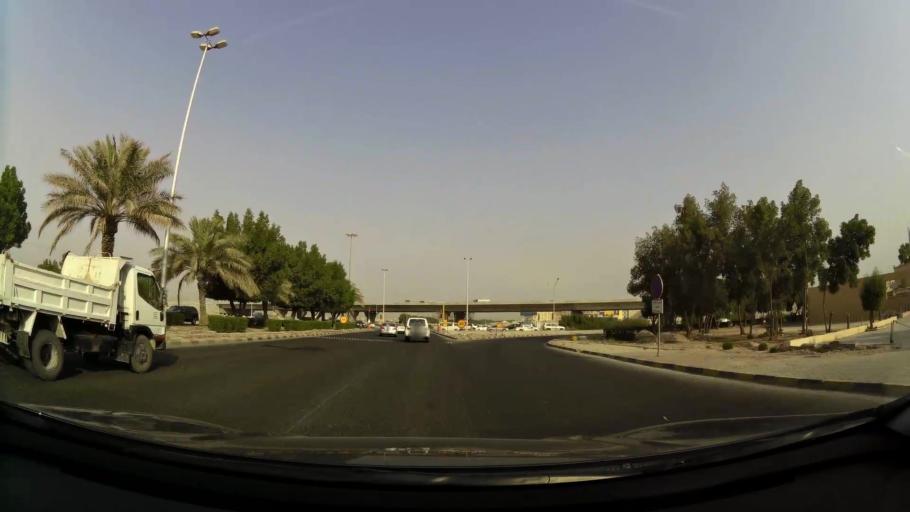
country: KW
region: Al Asimah
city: Ar Rabiyah
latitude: 29.3186
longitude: 47.8045
